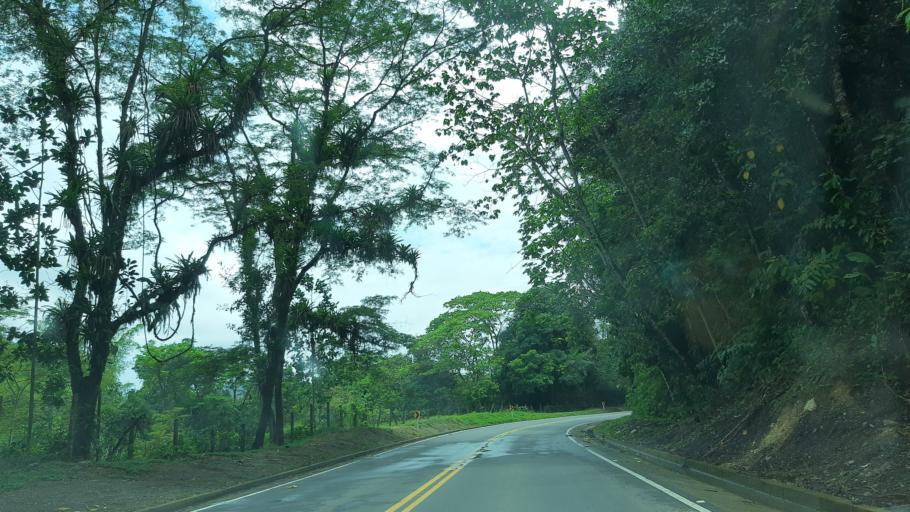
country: CO
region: Boyaca
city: San Luis de Gaceno
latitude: 4.8311
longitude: -73.1550
